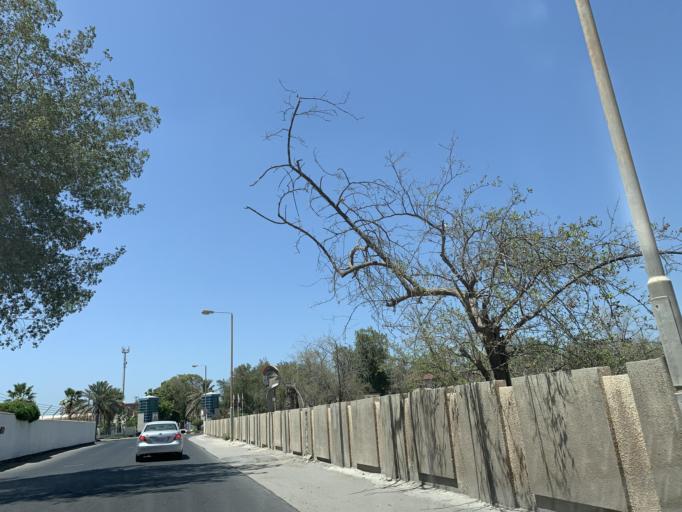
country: BH
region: Manama
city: Jidd Hafs
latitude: 26.2198
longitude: 50.4900
